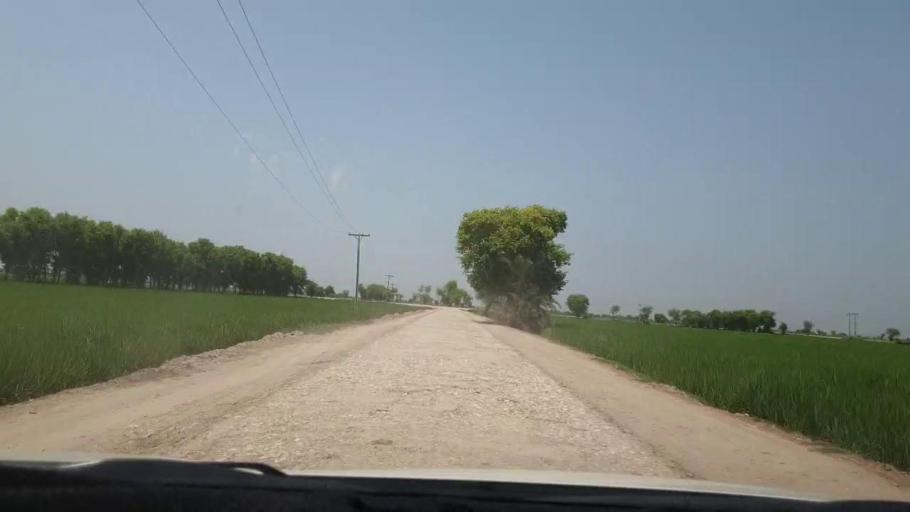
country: PK
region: Sindh
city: Radhan
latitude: 27.2489
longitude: 67.9834
